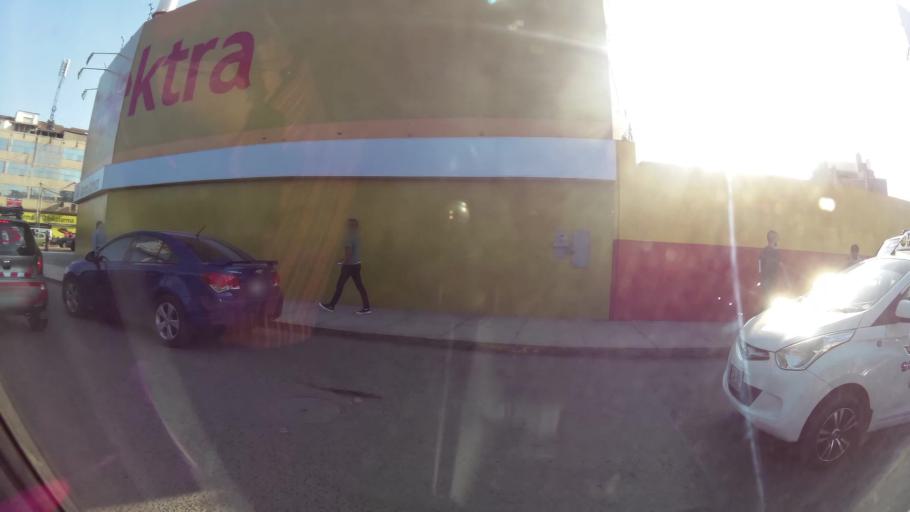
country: PE
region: Lambayeque
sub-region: Provincia de Chiclayo
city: Chiclayo
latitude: -6.7708
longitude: -79.8452
